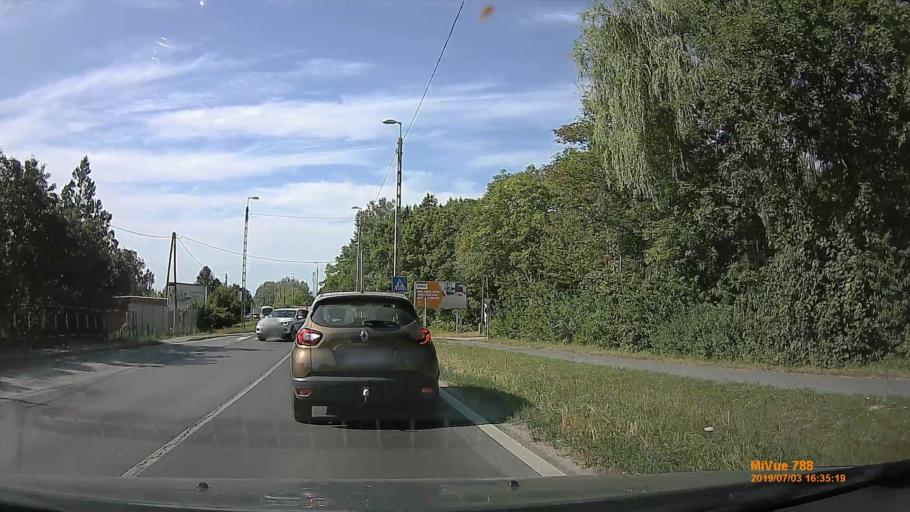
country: HU
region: Gyor-Moson-Sopron
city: Gyor
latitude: 47.7143
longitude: 17.6364
